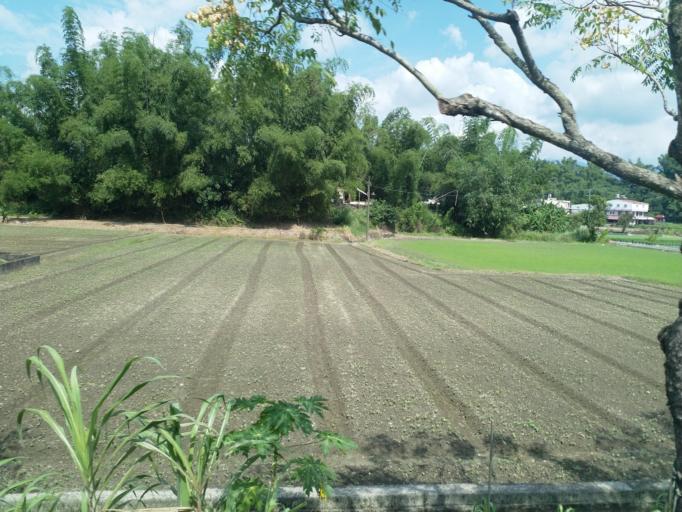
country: TW
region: Taiwan
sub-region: Pingtung
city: Pingtung
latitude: 22.8817
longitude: 120.5591
